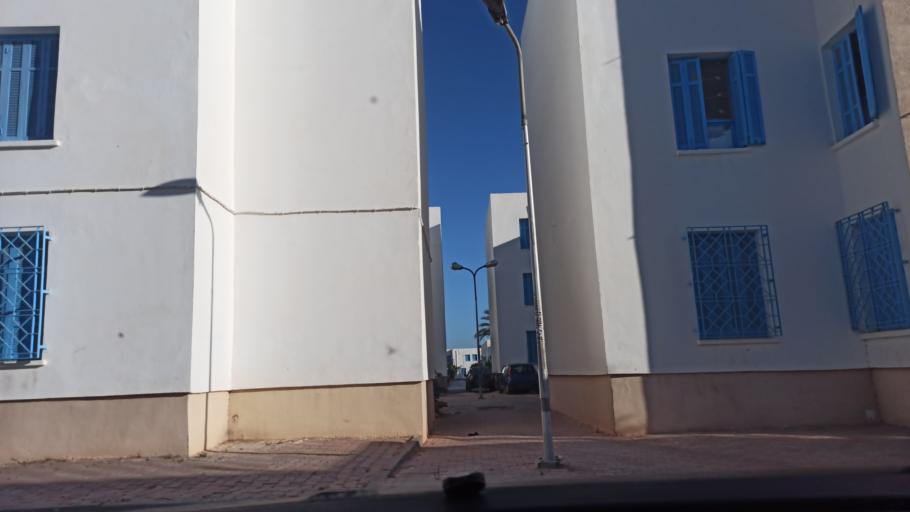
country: TN
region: Tunis
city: La Goulette
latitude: 36.8516
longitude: 10.2566
